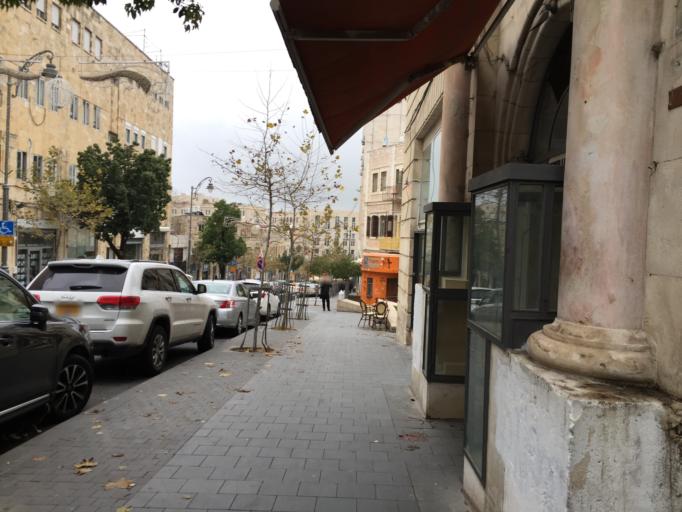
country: IL
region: Jerusalem
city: West Jerusalem
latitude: 31.7799
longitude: 35.2219
